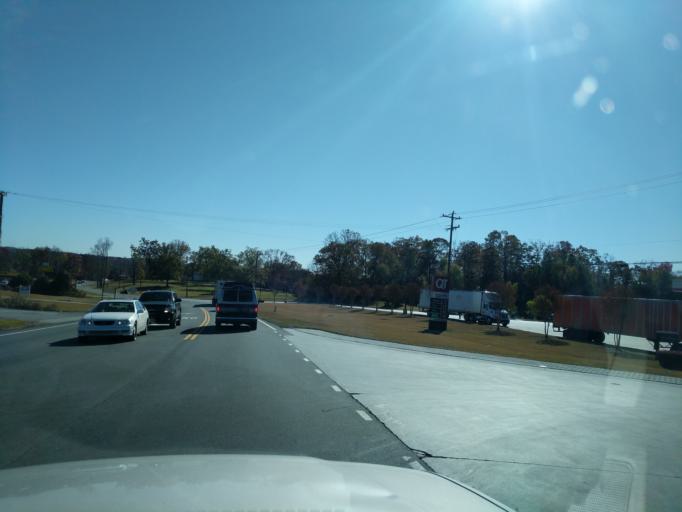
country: US
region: South Carolina
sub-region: Anderson County
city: Northlake
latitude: 34.5774
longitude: -82.6913
